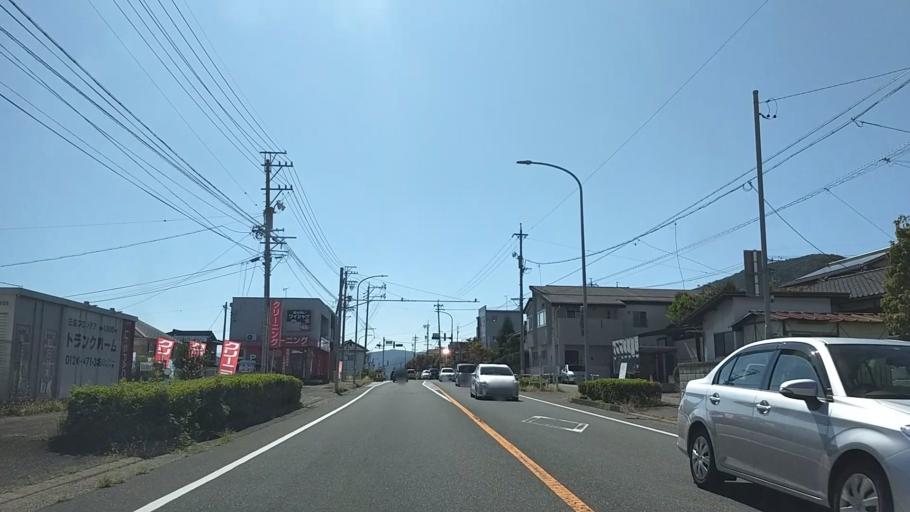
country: JP
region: Nagano
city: Nagano-shi
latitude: 36.6401
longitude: 138.1755
